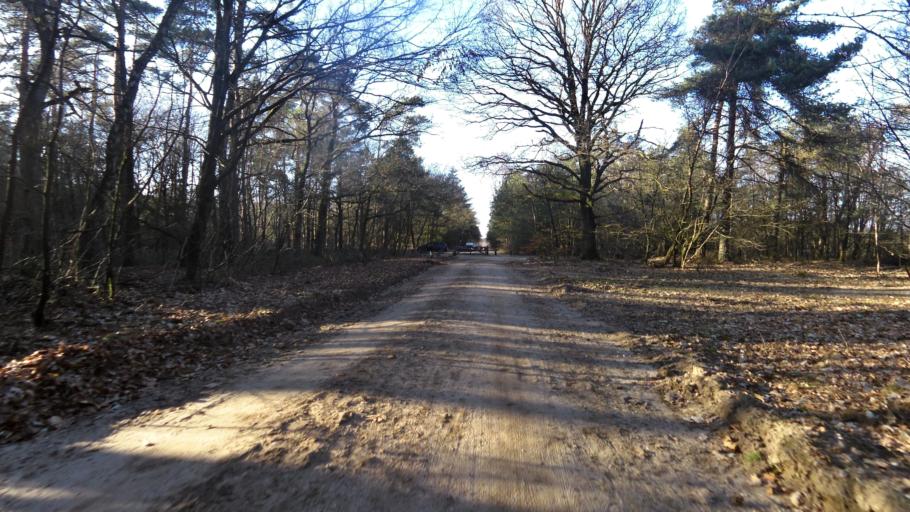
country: NL
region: Gelderland
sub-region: Gemeente Ermelo
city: Ermelo
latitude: 52.2757
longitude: 5.6753
